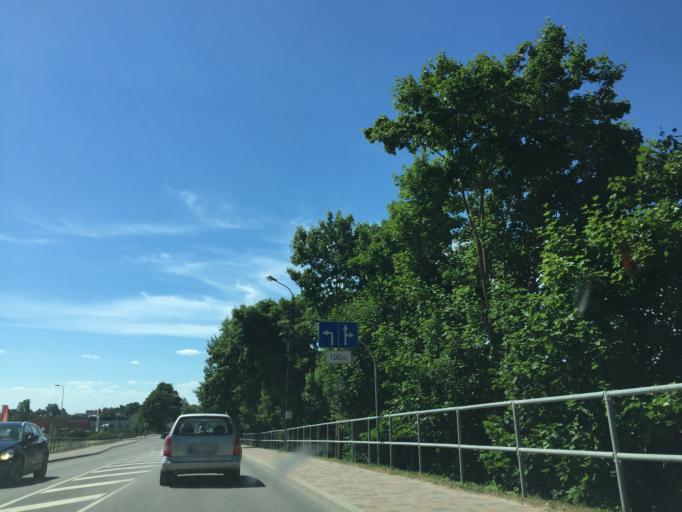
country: LV
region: Jekabpils Rajons
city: Jekabpils
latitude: 56.4965
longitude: 25.8777
